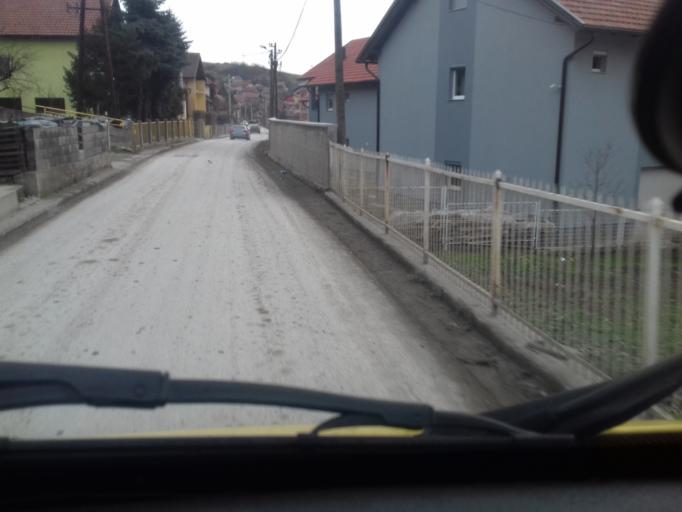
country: BA
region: Federation of Bosnia and Herzegovina
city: Zenica
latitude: 44.2298
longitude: 17.9081
